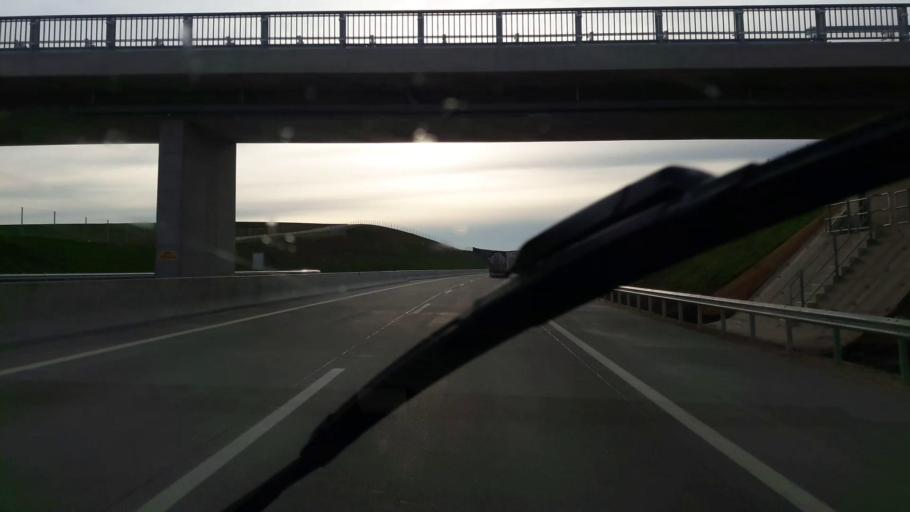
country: AT
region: Lower Austria
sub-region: Politischer Bezirk Mistelbach
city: Wilfersdorf
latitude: 48.6107
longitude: 16.6730
